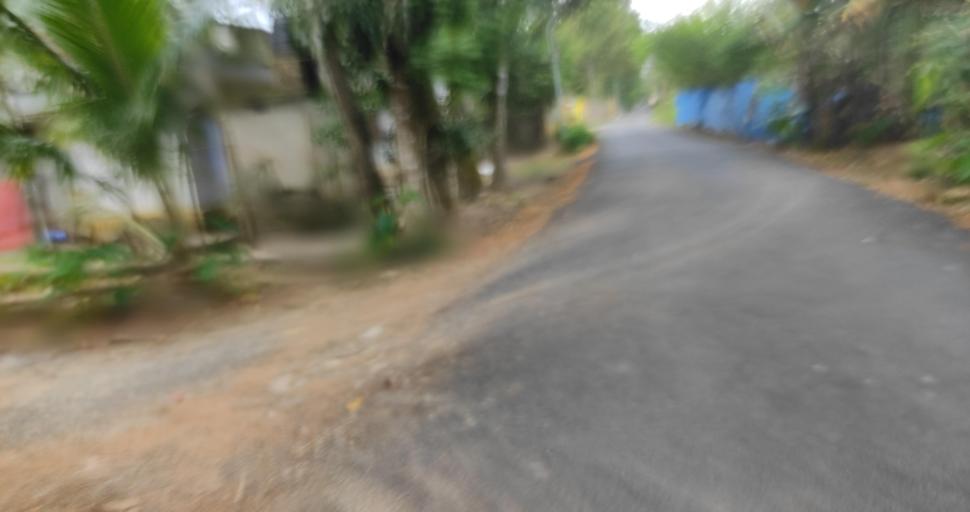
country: IN
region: Kerala
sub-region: Alappuzha
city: Shertallai
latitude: 9.6595
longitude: 76.3316
